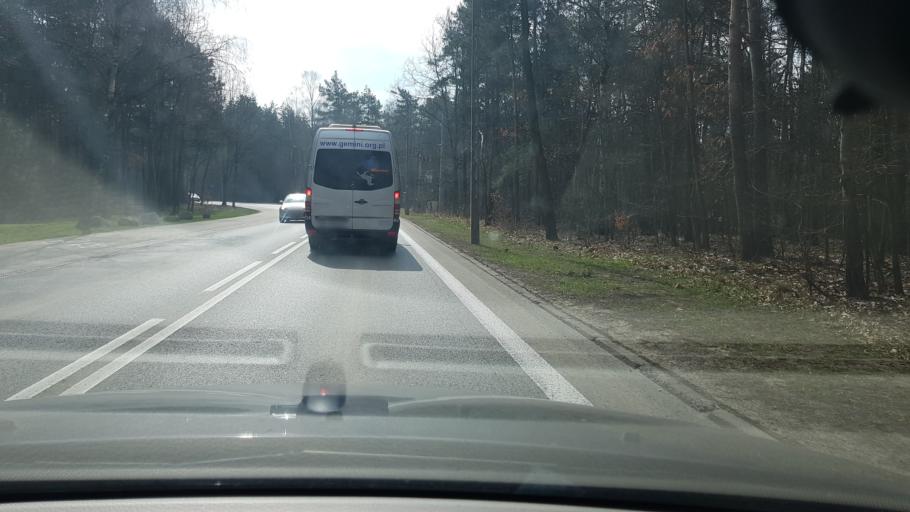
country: PL
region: Masovian Voivodeship
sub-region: Warszawa
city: Wesola
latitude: 52.2374
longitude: 21.2221
